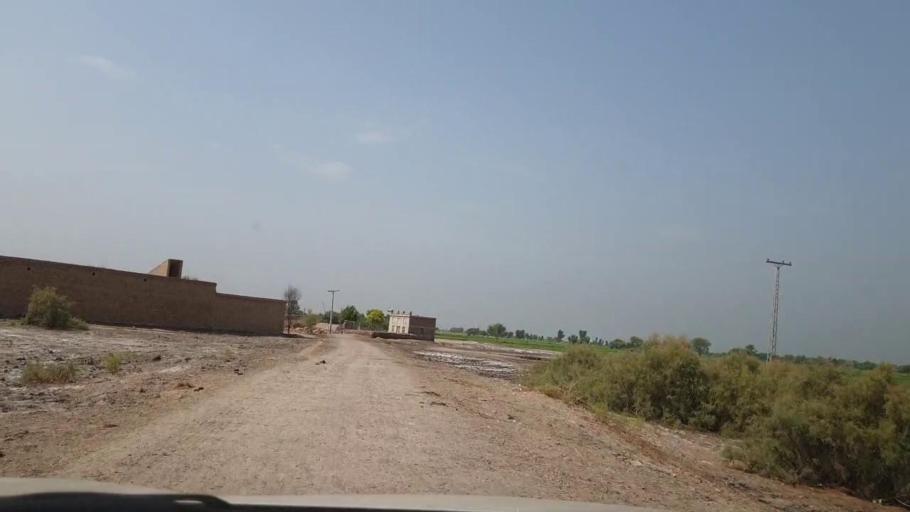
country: PK
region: Sindh
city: Dokri
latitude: 27.4170
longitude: 68.2038
